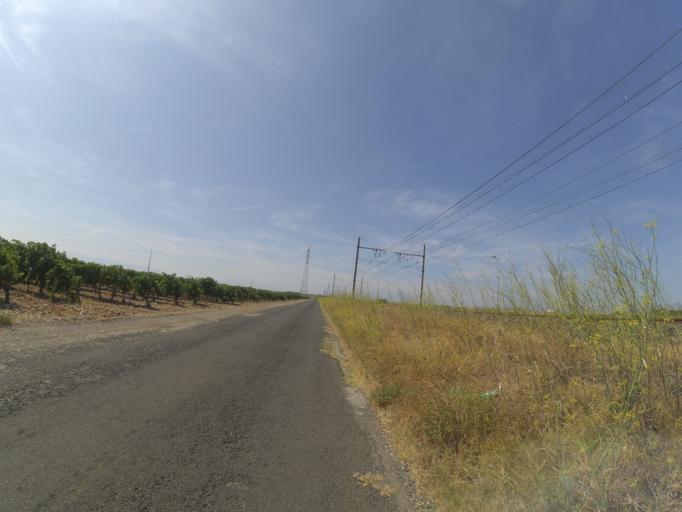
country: FR
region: Languedoc-Roussillon
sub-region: Departement des Pyrenees-Orientales
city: Salses-le-Chateau
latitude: 42.7999
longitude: 2.9021
